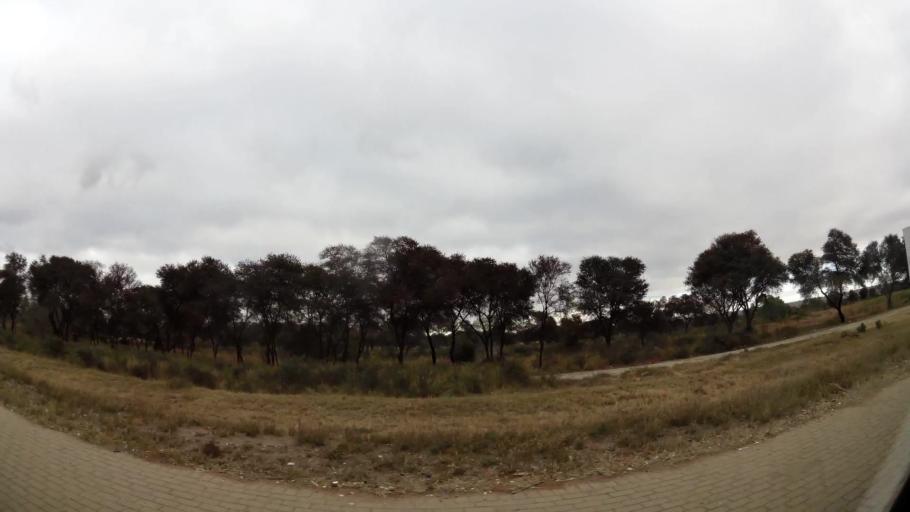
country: ZA
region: Limpopo
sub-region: Capricorn District Municipality
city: Polokwane
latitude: -23.8996
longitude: 29.4396
